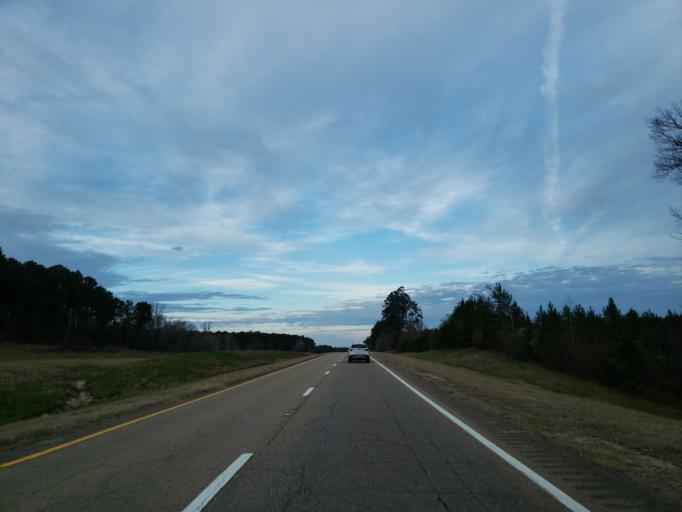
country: US
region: Mississippi
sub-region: Lauderdale County
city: Meridian Station
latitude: 32.4789
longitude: -88.5998
